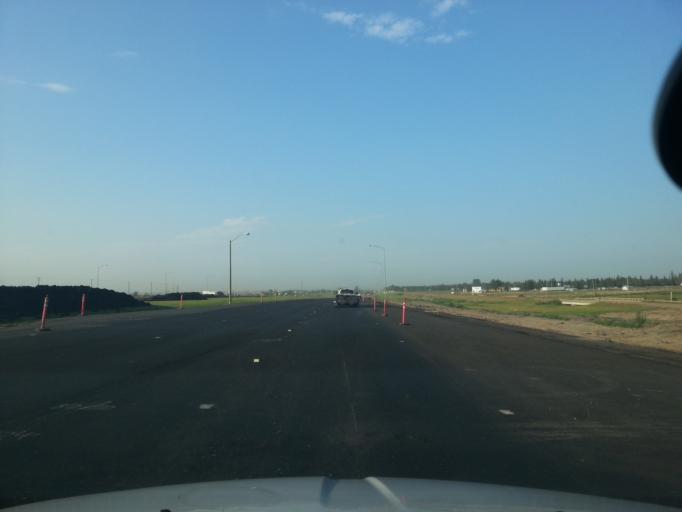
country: CA
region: Alberta
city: Beaumont
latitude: 53.3884
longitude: -113.5155
